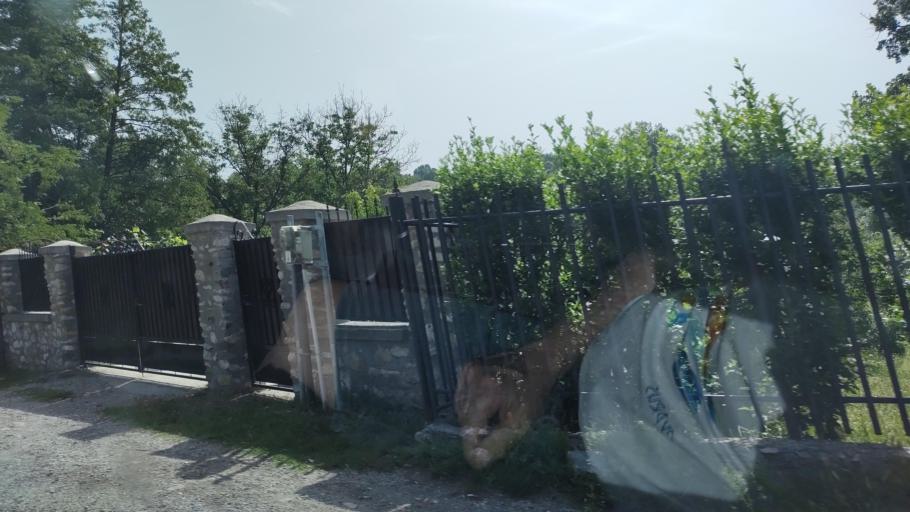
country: RO
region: Mehedinti
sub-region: Comuna Eselnita
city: Eselnita
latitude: 44.7198
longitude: 22.3631
